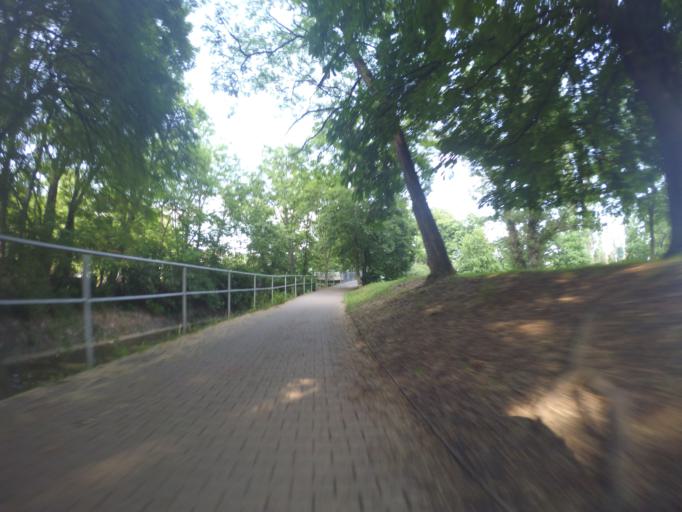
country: CZ
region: Praha
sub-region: Praha 8
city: Liben
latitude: 50.1093
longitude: 14.4854
